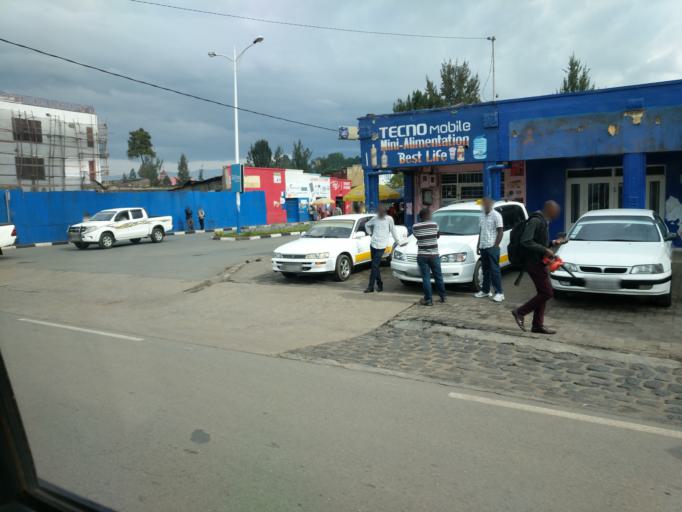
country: RW
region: Northern Province
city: Musanze
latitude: -1.5089
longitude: 29.6423
